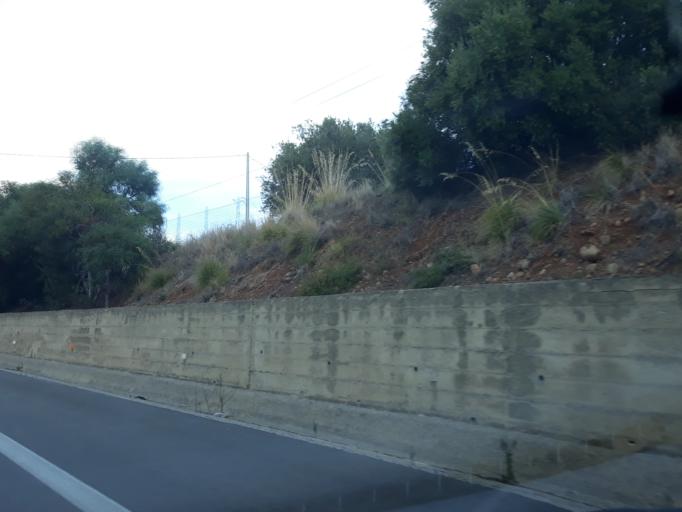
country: IT
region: Sicily
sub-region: Palermo
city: Termini Imerese
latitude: 37.9818
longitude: 13.6673
